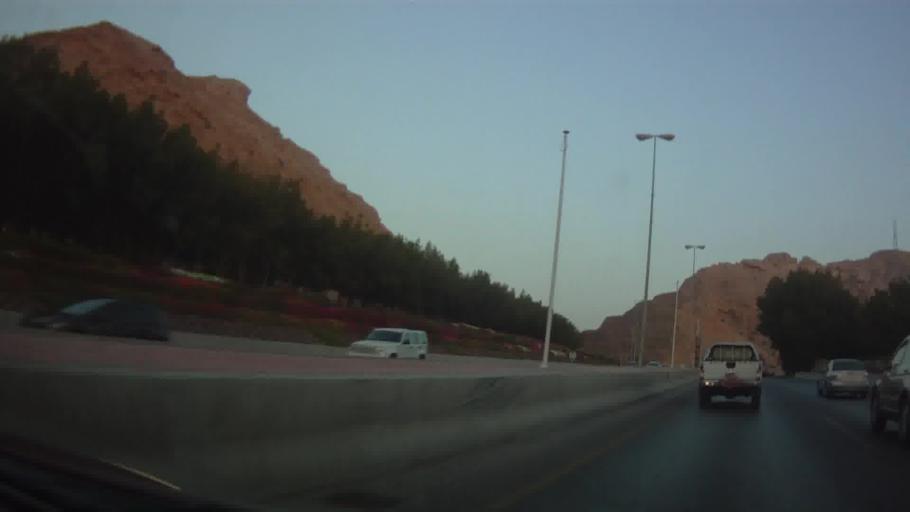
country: OM
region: Muhafazat Masqat
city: Muscat
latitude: 23.6163
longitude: 58.5256
